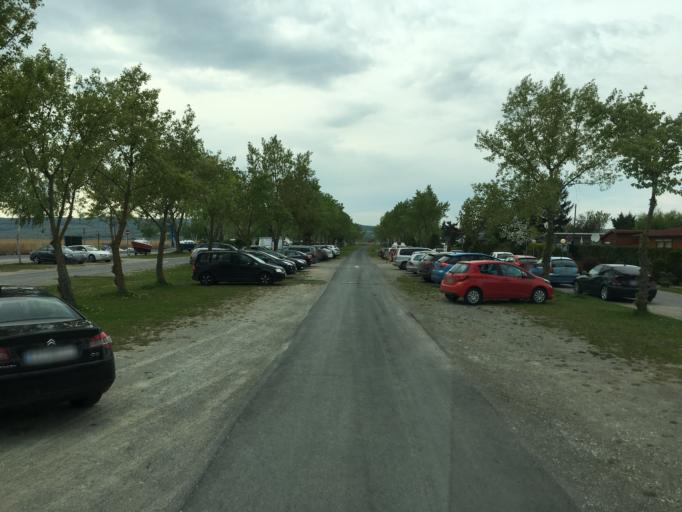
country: AT
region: Burgenland
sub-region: Politischer Bezirk Neusiedl am See
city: Winden am See
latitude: 47.9179
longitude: 16.7641
